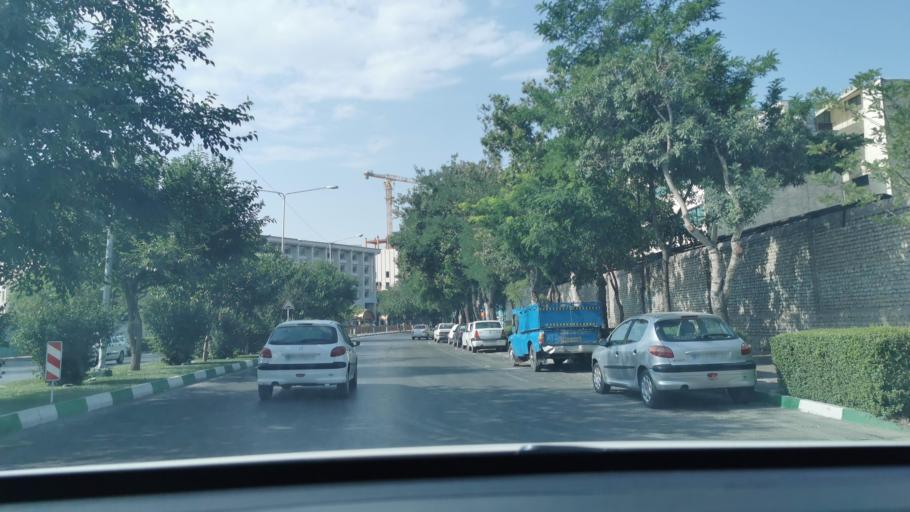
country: IR
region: Razavi Khorasan
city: Mashhad
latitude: 36.3217
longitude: 59.5631
